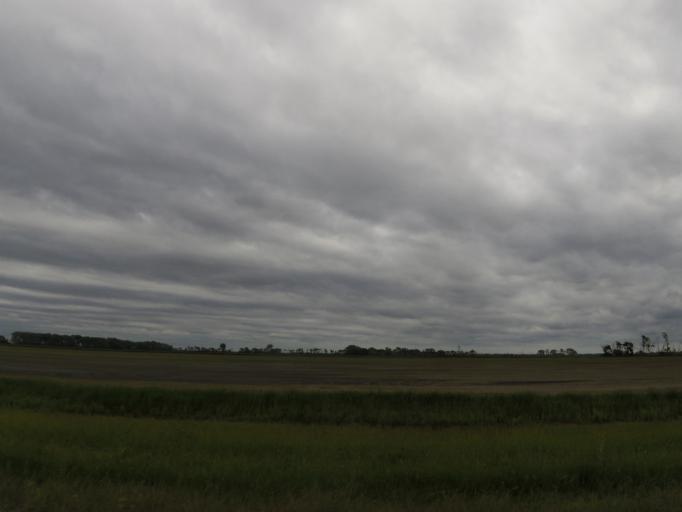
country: US
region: North Dakota
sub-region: Walsh County
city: Grafton
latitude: 48.5226
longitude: -97.4477
